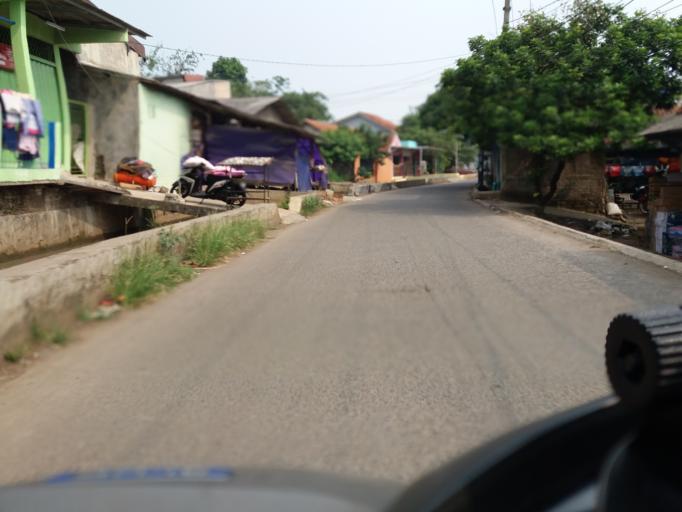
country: ID
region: West Java
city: Cibinong
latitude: -6.4434
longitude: 106.8628
